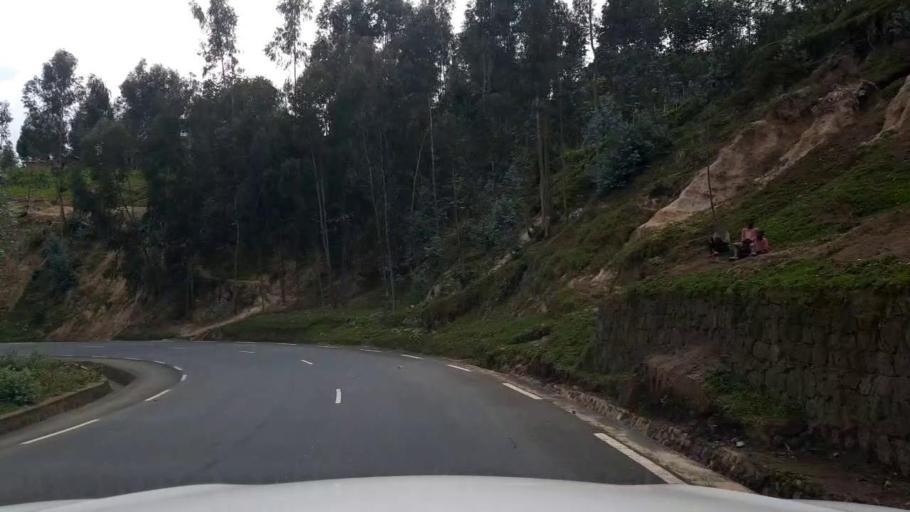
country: RW
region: Northern Province
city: Musanze
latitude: -1.6792
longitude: 29.5150
